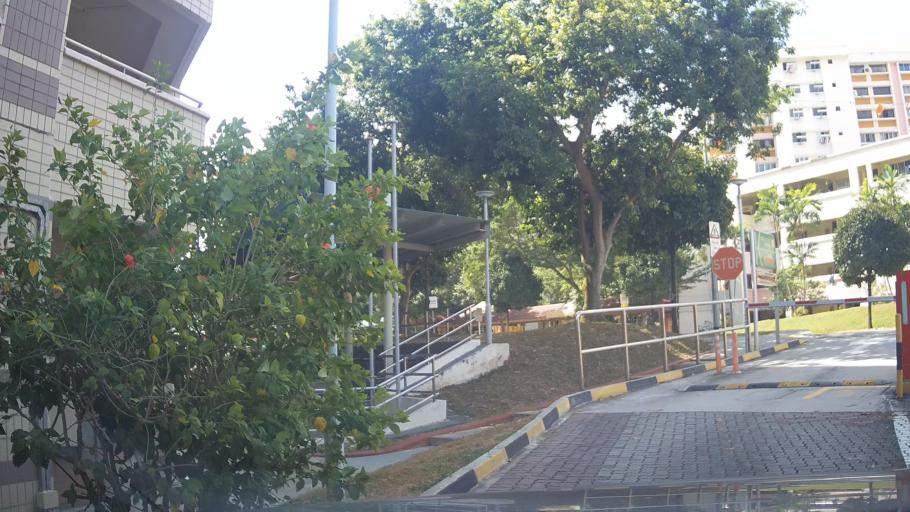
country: SG
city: Singapore
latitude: 1.3556
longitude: 103.9504
